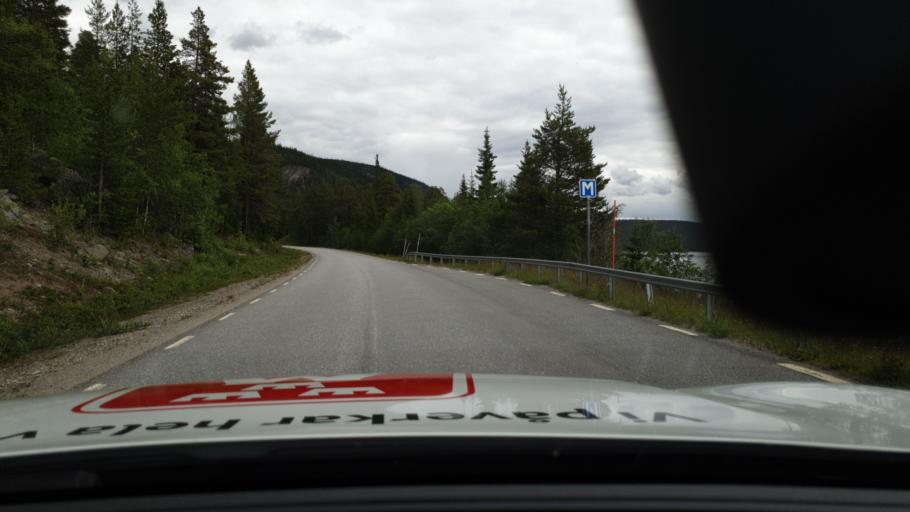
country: SE
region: Norrbotten
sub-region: Arjeplogs Kommun
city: Arjeplog
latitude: 66.8966
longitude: 17.8443
